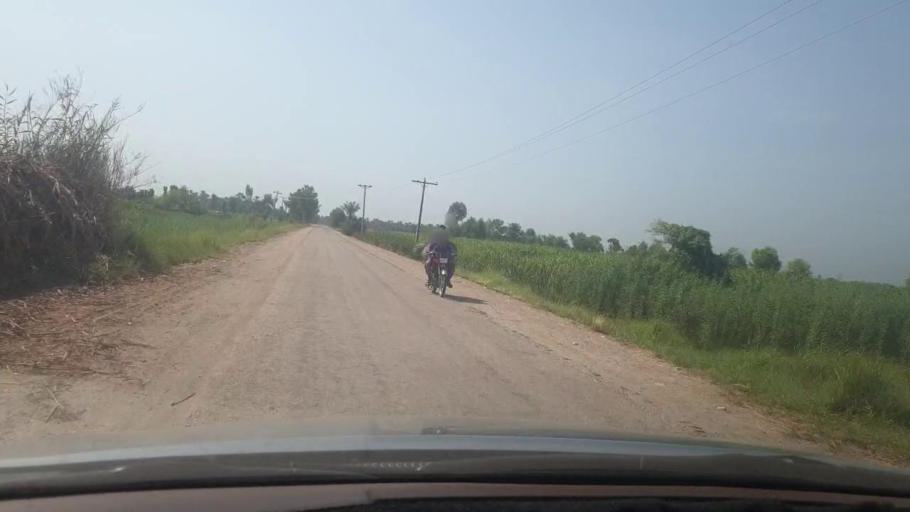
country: PK
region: Sindh
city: Ranipur
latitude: 27.2921
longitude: 68.5748
